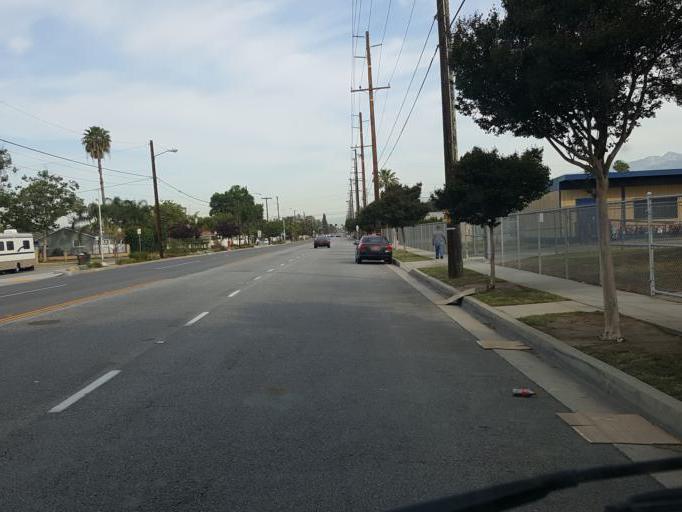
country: US
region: California
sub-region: Los Angeles County
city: West Puente Valley
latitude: 34.0377
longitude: -117.9638
